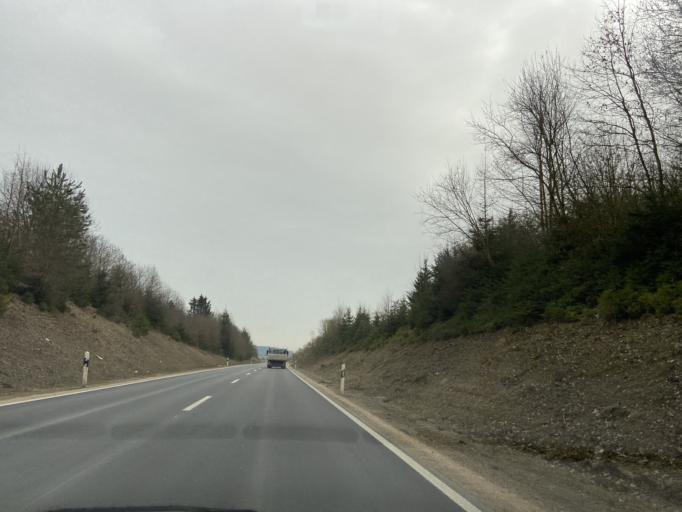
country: DE
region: Baden-Wuerttemberg
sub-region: Tuebingen Region
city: Ostrach
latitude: 47.9542
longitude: 9.3971
